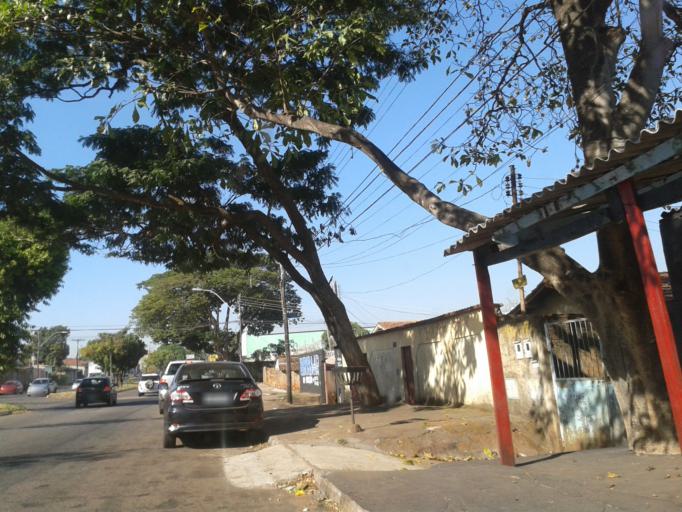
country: BR
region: Goias
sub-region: Goiania
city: Goiania
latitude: -16.6991
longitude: -49.3174
